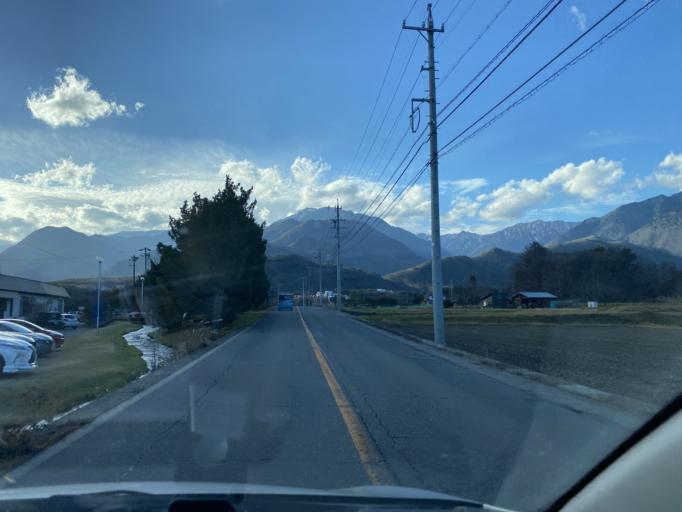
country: JP
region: Nagano
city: Omachi
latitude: 36.5277
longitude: 137.8196
